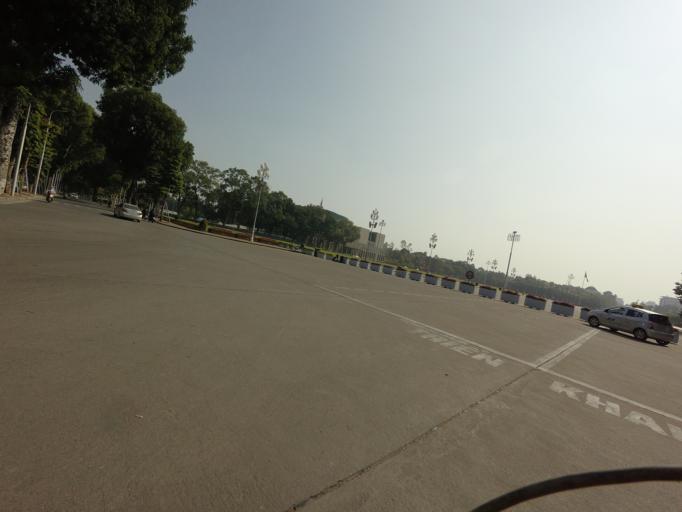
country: VN
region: Ha Noi
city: Hanoi
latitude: 21.0393
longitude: 105.8355
